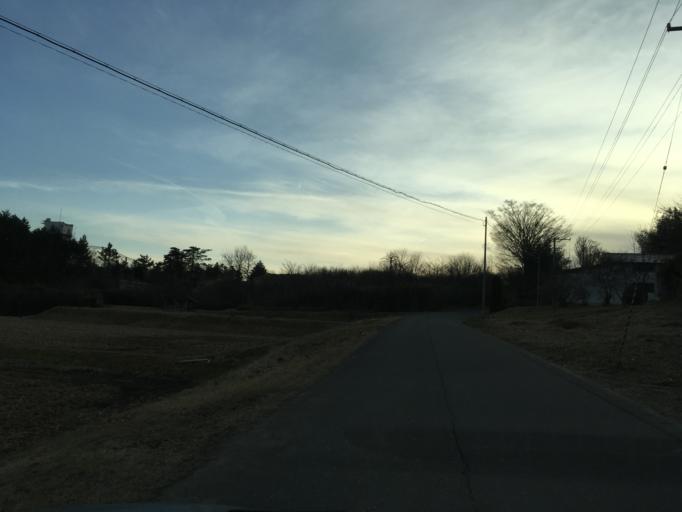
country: JP
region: Miyagi
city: Kogota
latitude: 38.6743
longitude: 141.0882
